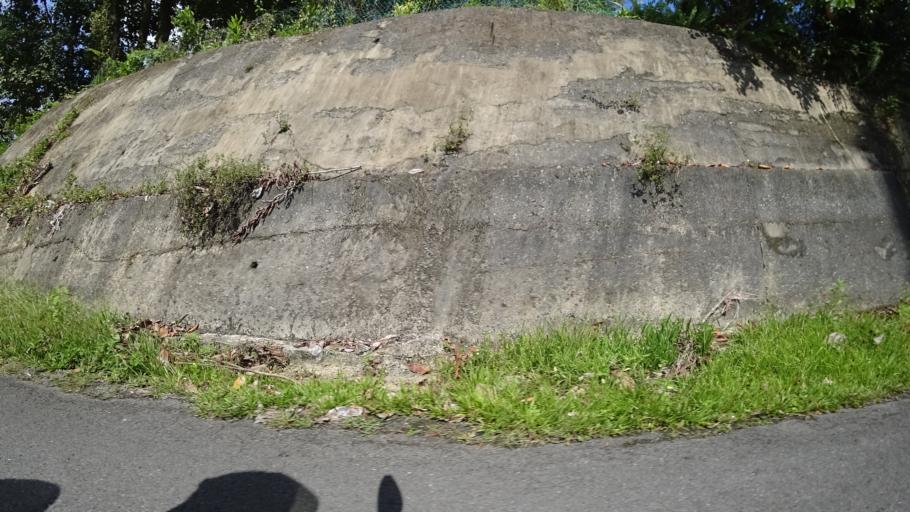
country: MY
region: Sarawak
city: Limbang
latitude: 4.7600
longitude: 115.0072
